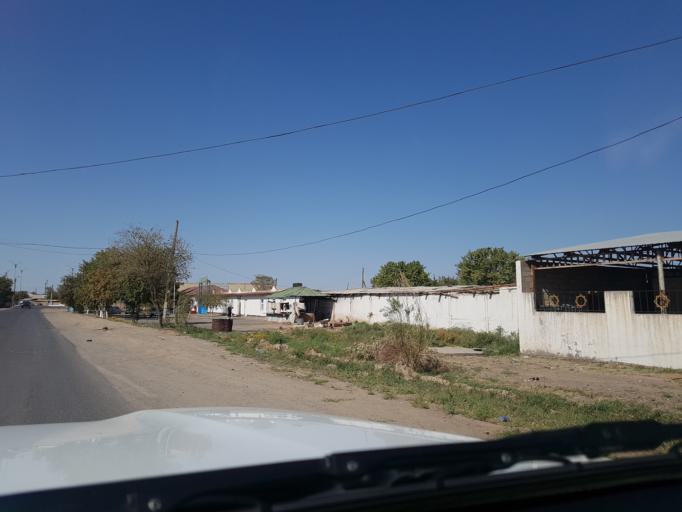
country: IR
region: Razavi Khorasan
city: Sarakhs
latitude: 36.5216
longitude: 61.2179
